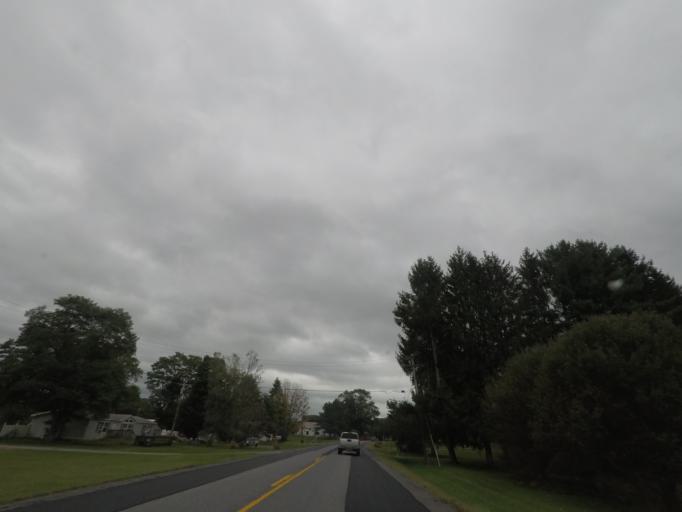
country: US
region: New York
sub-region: Rensselaer County
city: Hoosick Falls
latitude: 42.9514
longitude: -73.4088
